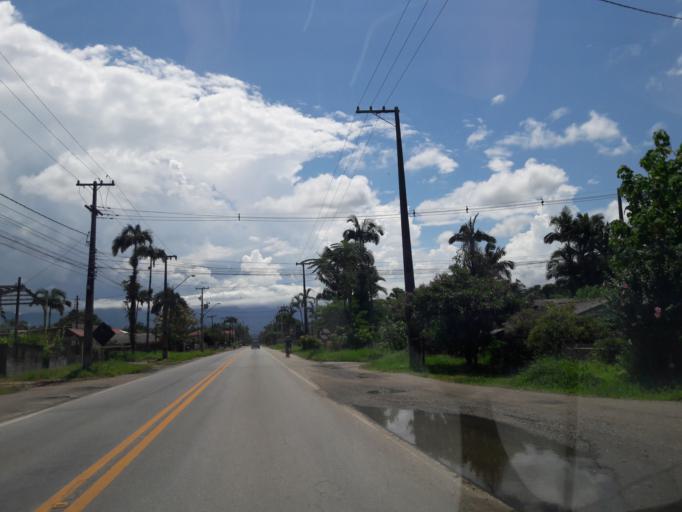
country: BR
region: Parana
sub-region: Antonina
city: Antonina
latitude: -25.4930
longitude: -48.8219
